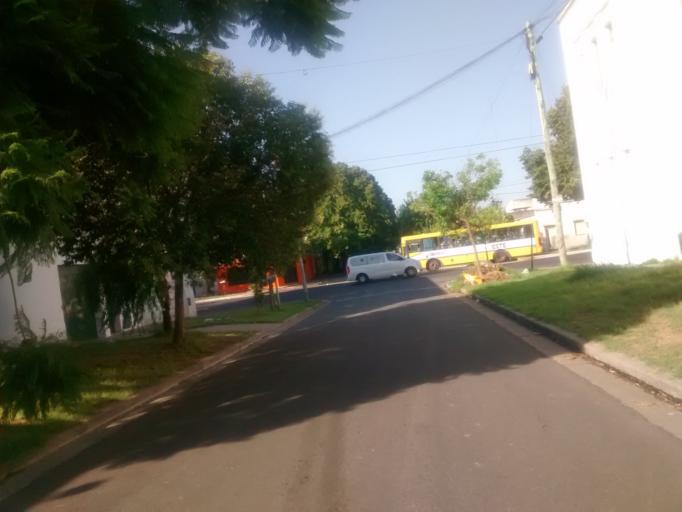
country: AR
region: Buenos Aires
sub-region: Partido de La Plata
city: La Plata
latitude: -34.9337
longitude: -57.9252
